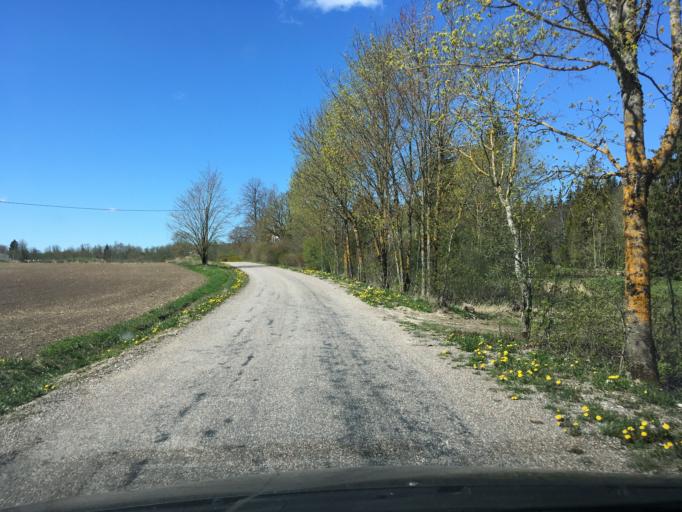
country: EE
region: Harju
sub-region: Rae vald
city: Vaida
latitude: 59.1980
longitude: 25.0598
